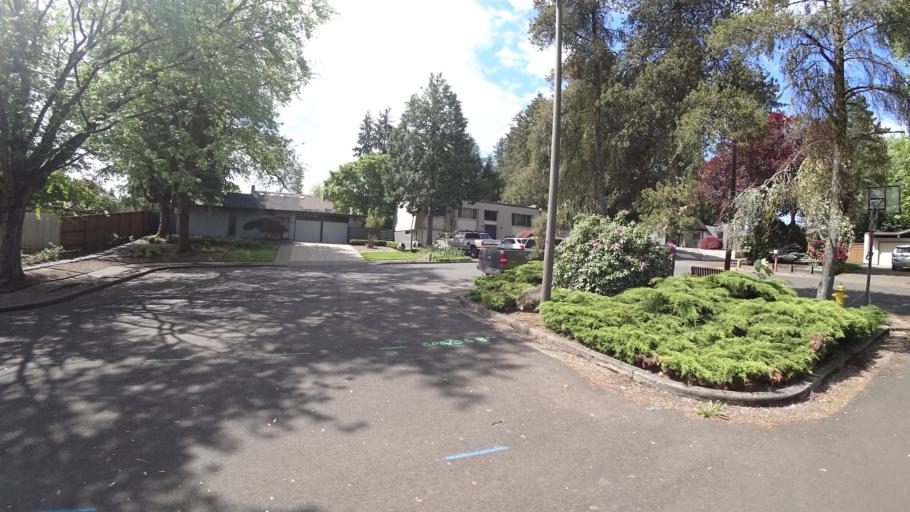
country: US
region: Oregon
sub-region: Washington County
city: Beaverton
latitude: 45.4693
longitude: -122.8119
